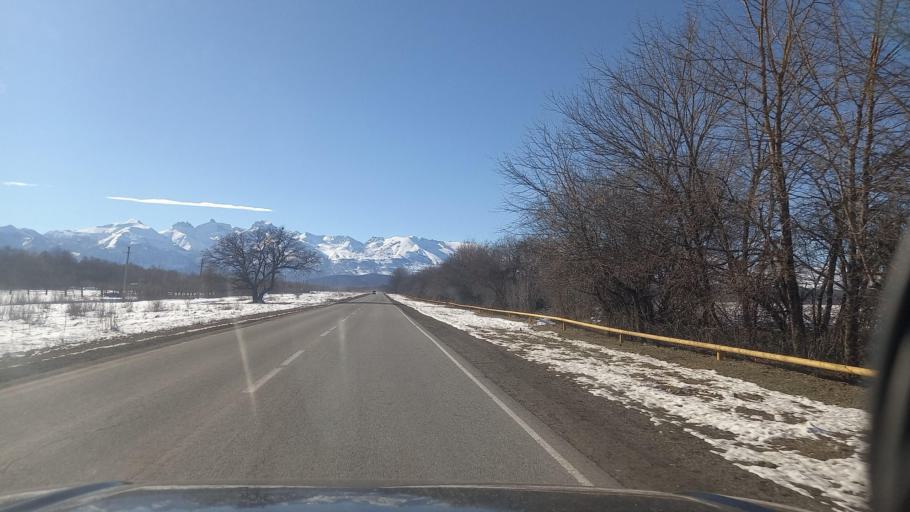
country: RU
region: North Ossetia
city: Chikola
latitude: 43.1736
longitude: 43.8734
